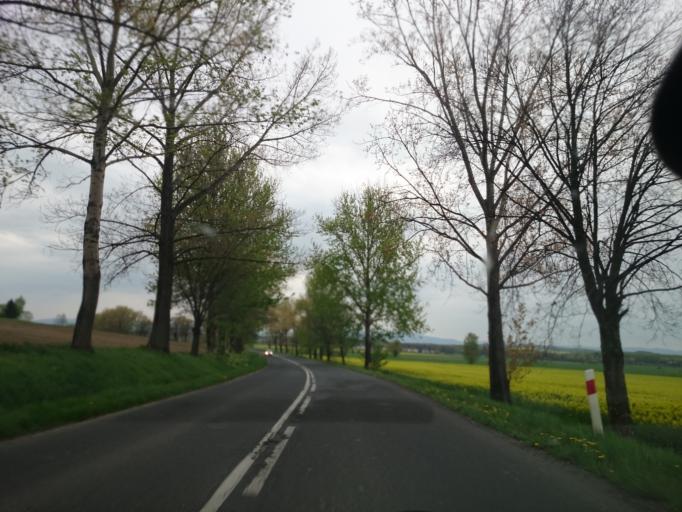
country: PL
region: Opole Voivodeship
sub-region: Powiat nyski
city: Nysa
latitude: 50.4240
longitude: 17.3391
